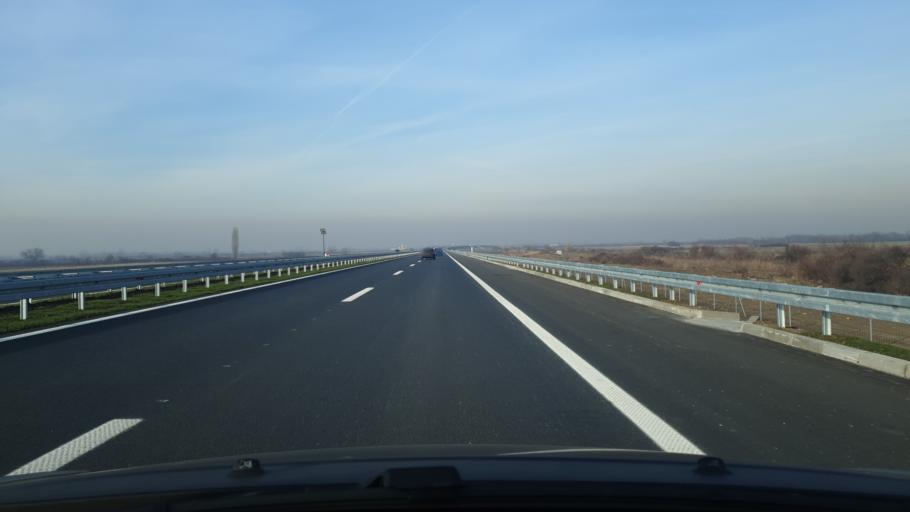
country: RS
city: Boljevci
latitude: 44.7063
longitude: 20.2619
